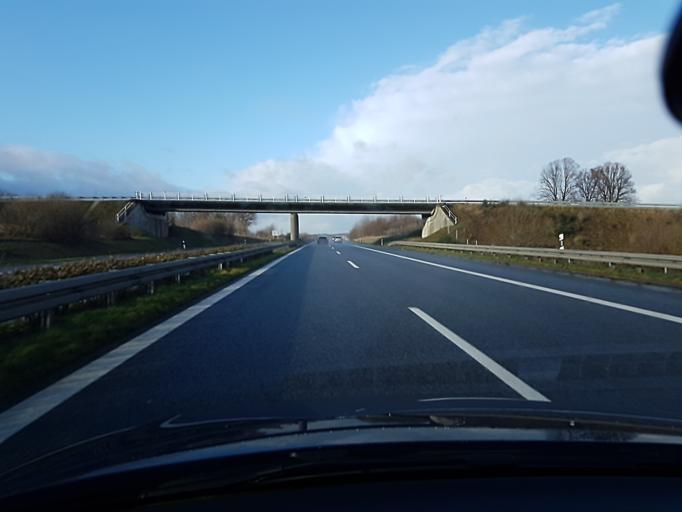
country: DE
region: Mecklenburg-Vorpommern
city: Tessin
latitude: 54.0175
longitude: 12.4365
